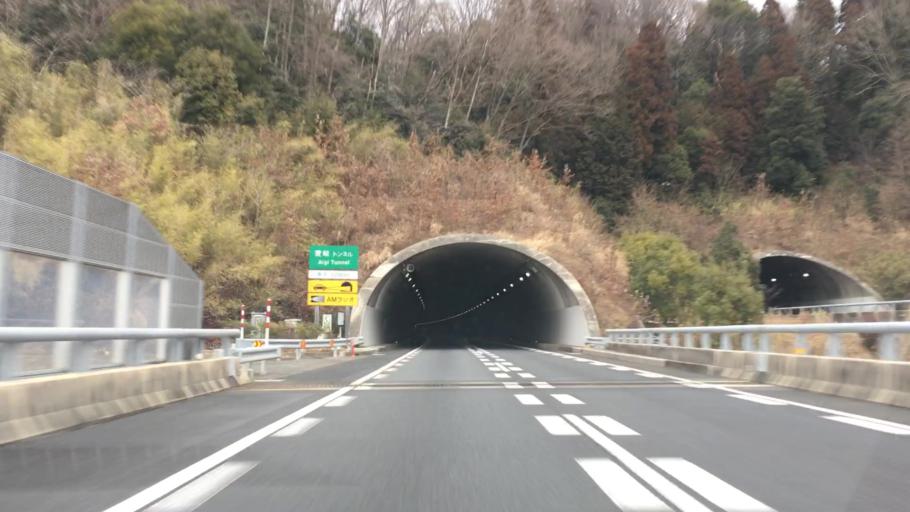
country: JP
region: Gifu
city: Tajimi
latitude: 35.2606
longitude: 137.1534
